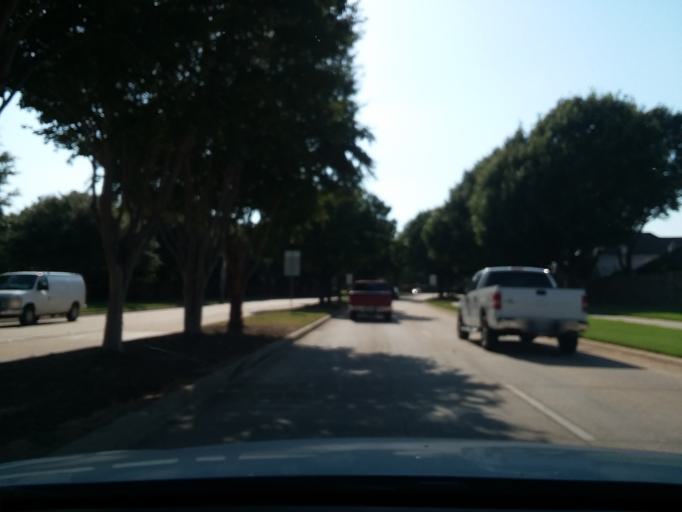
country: US
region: Texas
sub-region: Denton County
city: Flower Mound
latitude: 33.0268
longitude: -97.0912
